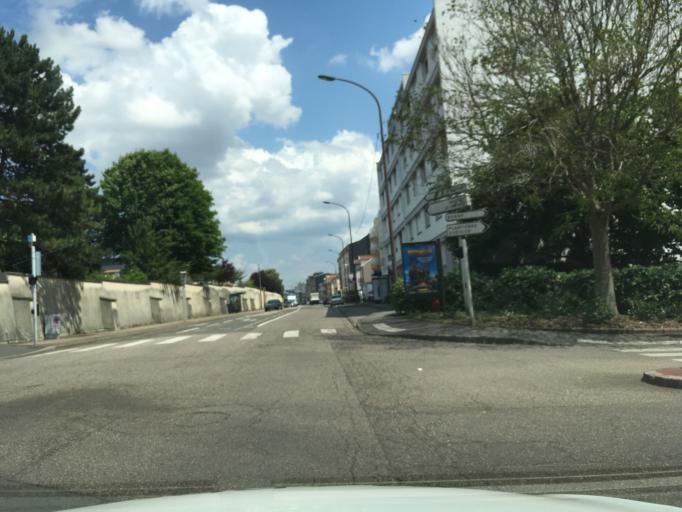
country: FR
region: Lorraine
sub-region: Departement de la Moselle
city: Saint-Julien-les-Metz
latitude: 49.1188
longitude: 6.2034
